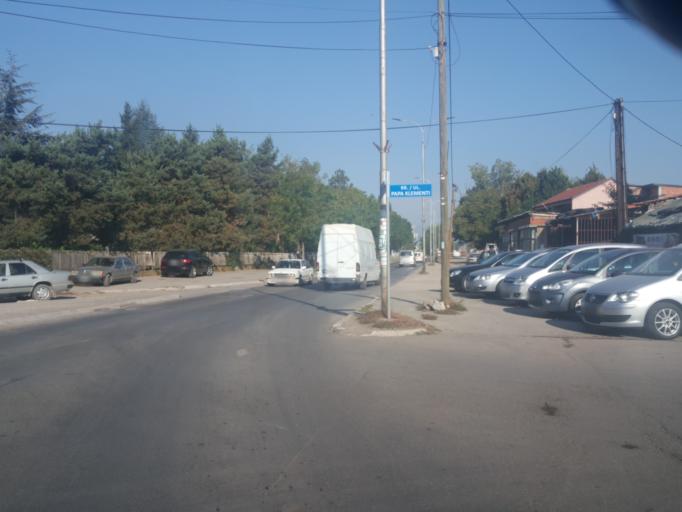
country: XK
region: Gjakova
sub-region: Komuna e Gjakoves
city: Gjakove
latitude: 42.3922
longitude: 20.4242
